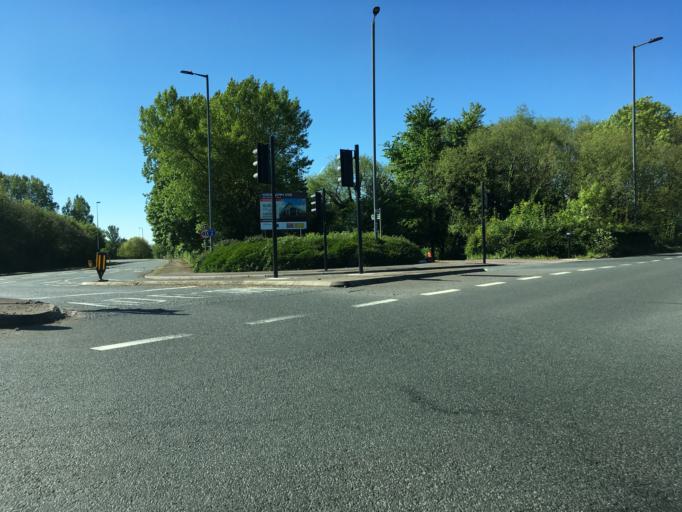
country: GB
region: England
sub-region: South Gloucestershire
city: Severn Beach
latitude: 51.5555
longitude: -2.6552
